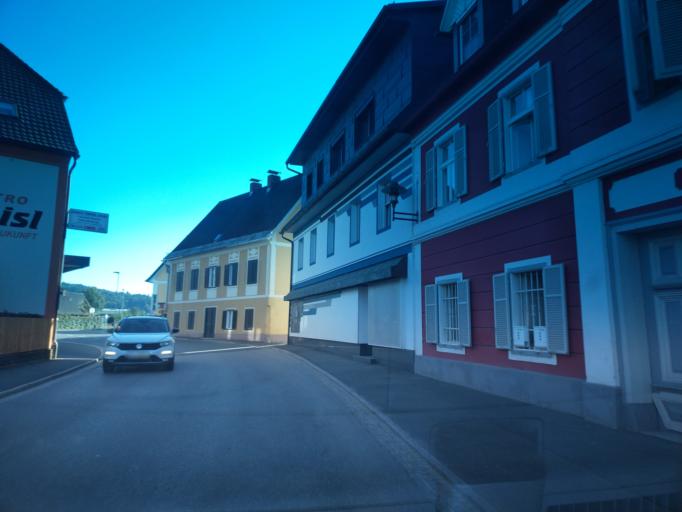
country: AT
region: Styria
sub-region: Politischer Bezirk Deutschlandsberg
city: Gross Sankt Florian
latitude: 46.8217
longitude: 15.3163
